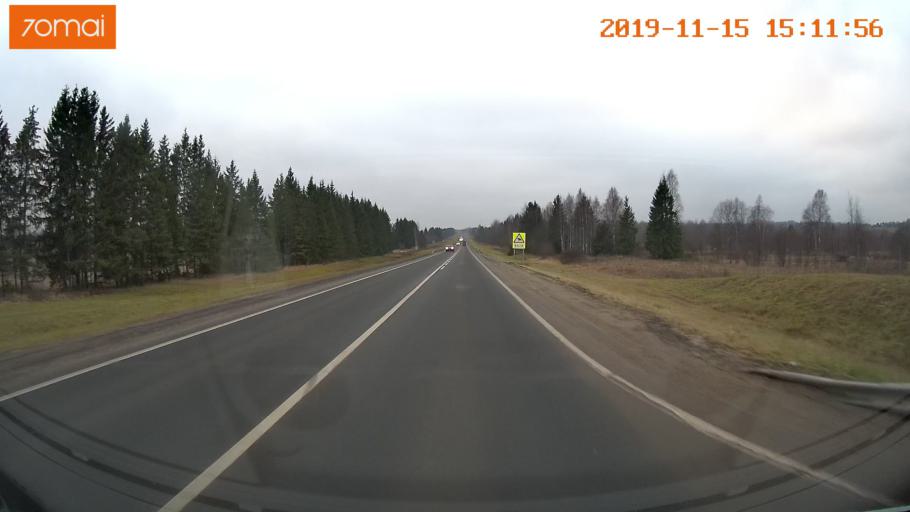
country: RU
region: Jaroslavl
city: Prechistoye
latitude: 58.3302
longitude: 40.2341
